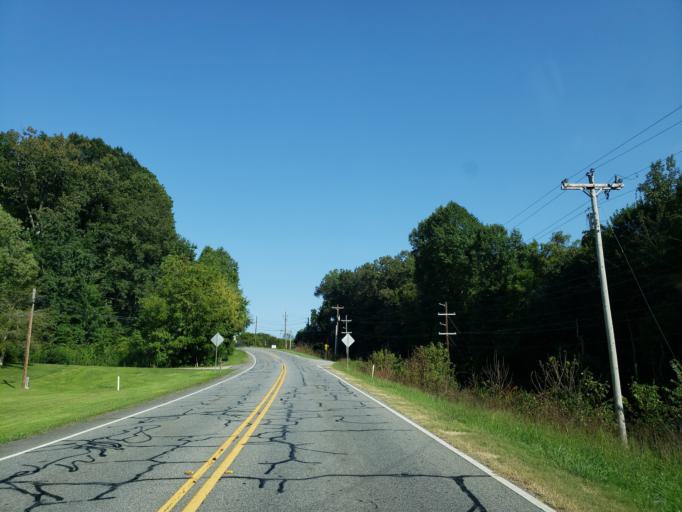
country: US
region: Georgia
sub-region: Catoosa County
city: Ringgold
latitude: 34.9054
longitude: -85.0754
